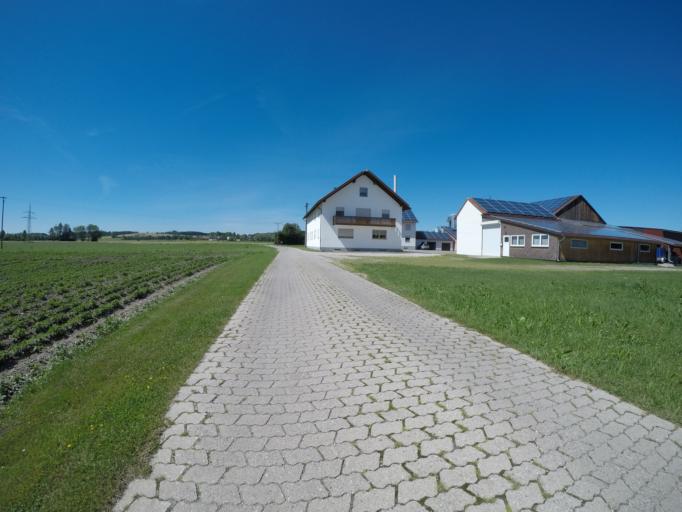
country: DE
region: Bavaria
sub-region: Upper Bavaria
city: Haag an der Amper
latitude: 48.4471
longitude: 11.7994
